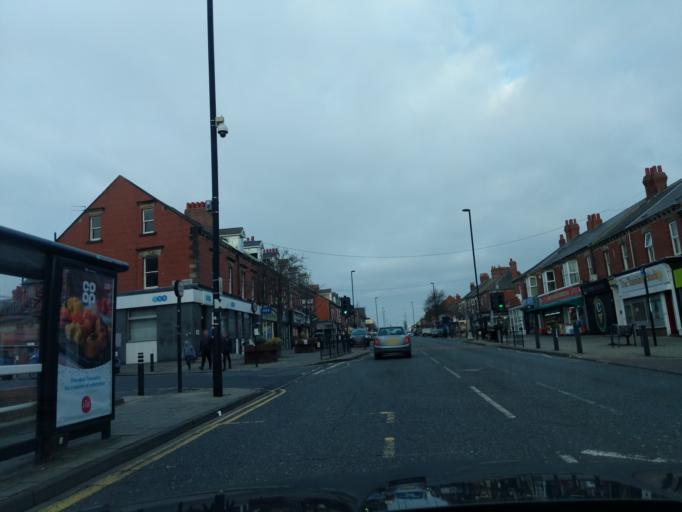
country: GB
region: England
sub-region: Gateshead
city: Felling
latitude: 54.9870
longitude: -1.5771
